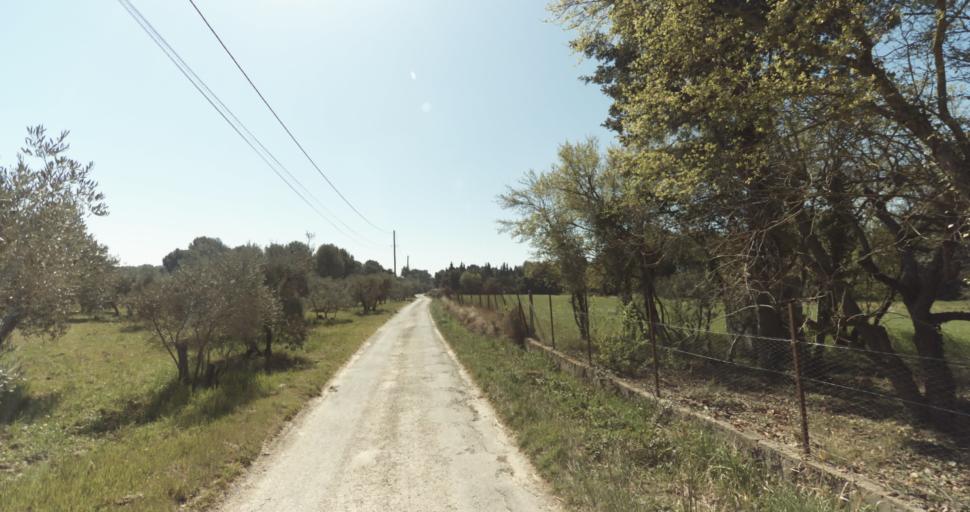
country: FR
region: Provence-Alpes-Cote d'Azur
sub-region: Departement des Bouches-du-Rhone
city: Pelissanne
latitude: 43.6167
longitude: 5.1572
